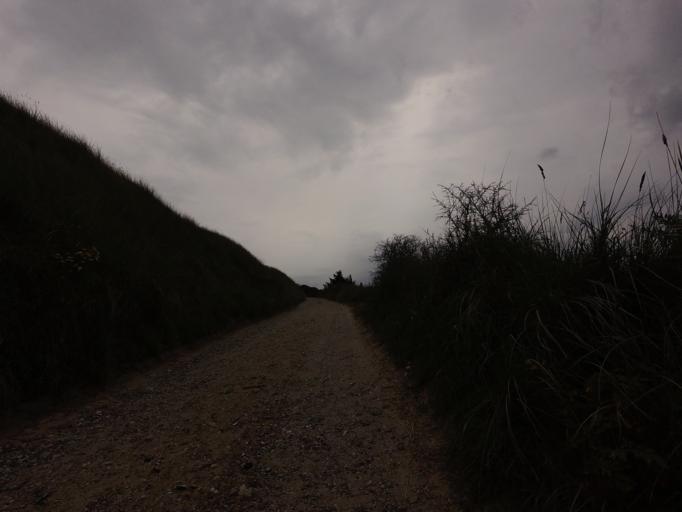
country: DK
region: North Denmark
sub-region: Jammerbugt Kommune
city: Pandrup
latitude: 57.3052
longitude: 9.6447
